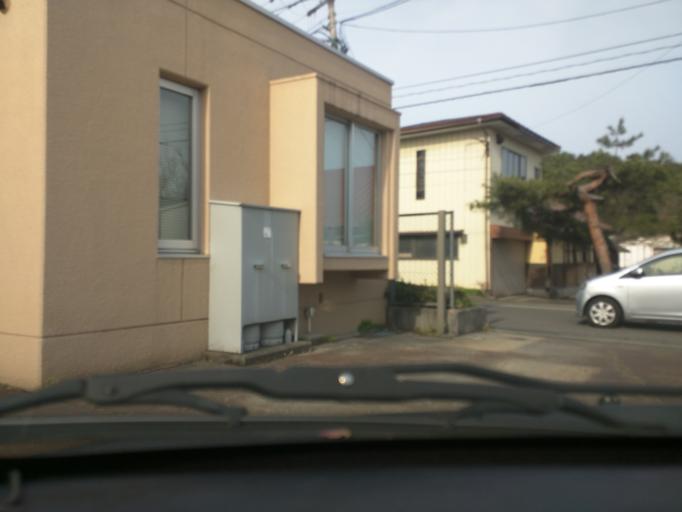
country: JP
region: Fukushima
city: Kitakata
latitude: 37.4504
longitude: 139.8895
